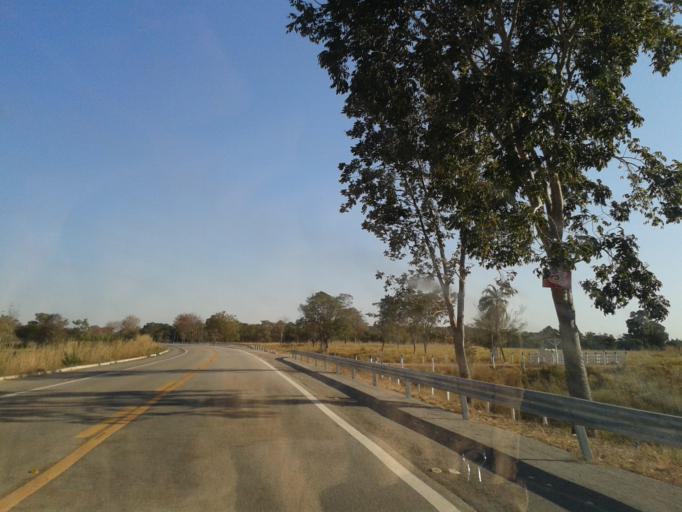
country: BR
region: Goias
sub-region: Mozarlandia
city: Mozarlandia
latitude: -15.1484
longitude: -50.5802
